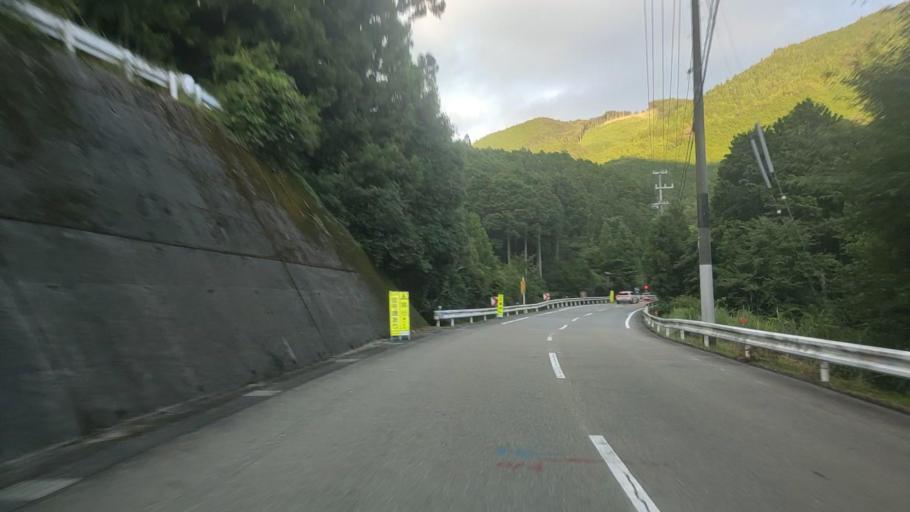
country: JP
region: Wakayama
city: Tanabe
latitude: 33.8306
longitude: 135.6469
